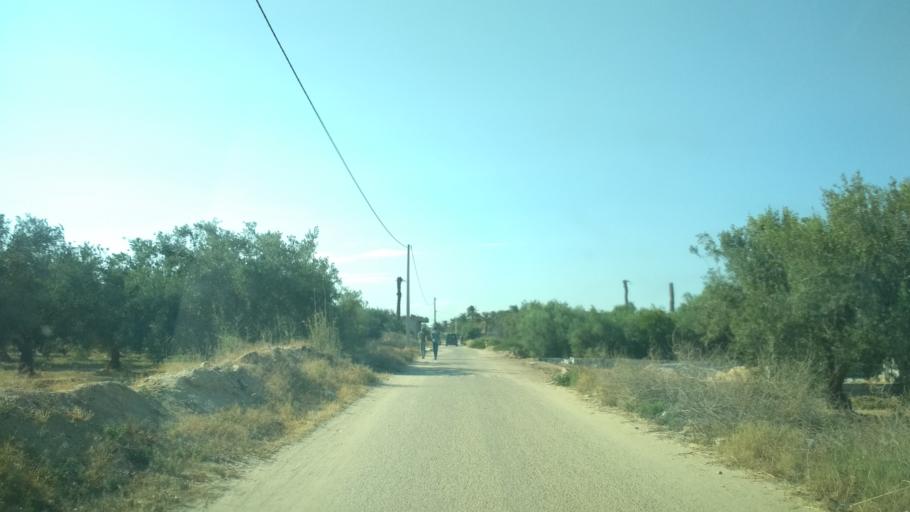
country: TN
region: Qabis
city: Gabes
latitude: 33.9531
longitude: 10.0600
